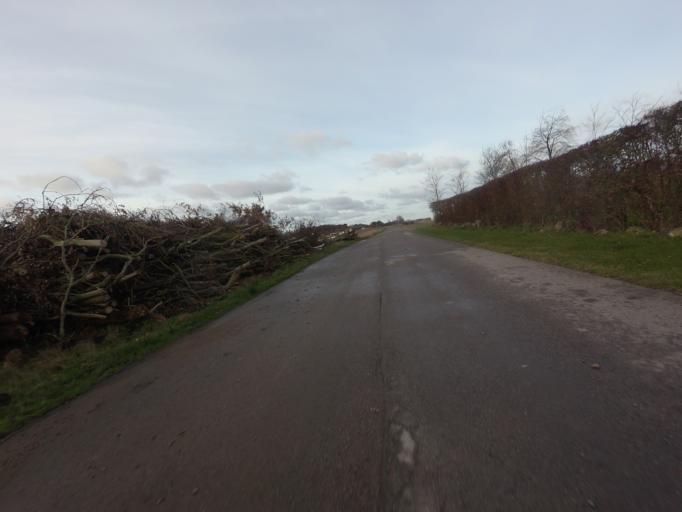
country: SE
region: Skane
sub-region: Hoganas Kommun
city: Hoganas
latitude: 56.1625
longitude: 12.5830
